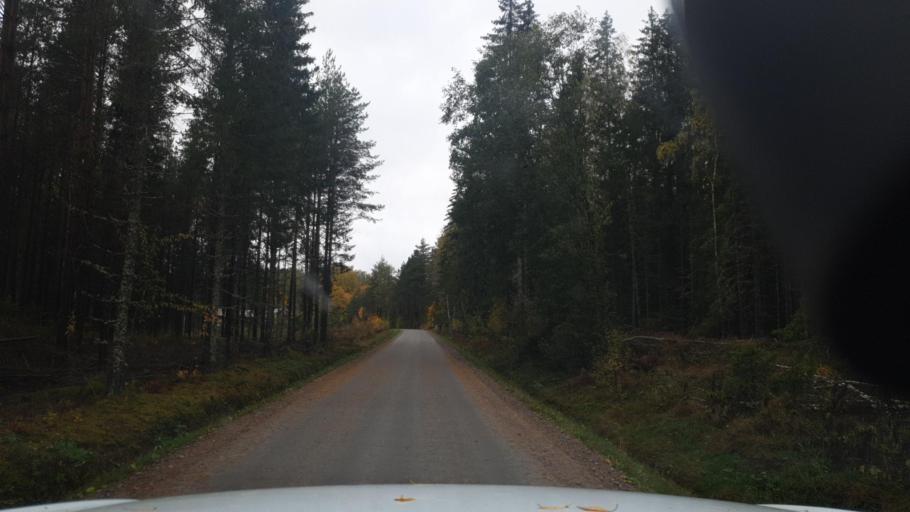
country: SE
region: Vaermland
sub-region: Karlstads Kommun
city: Edsvalla
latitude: 59.5427
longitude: 13.0020
